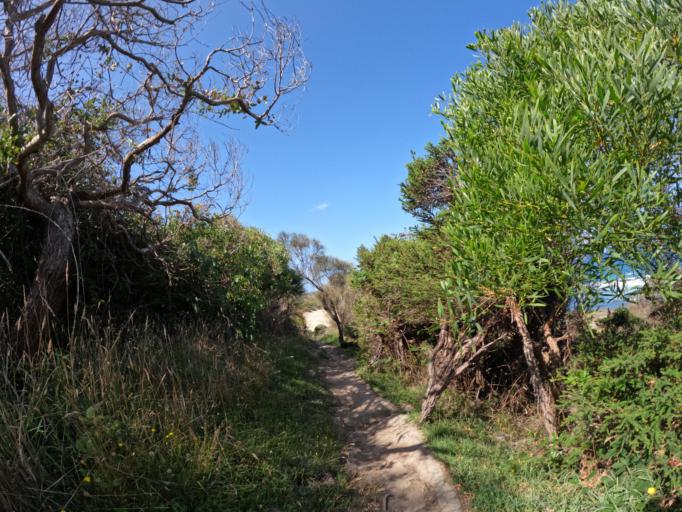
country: AU
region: Victoria
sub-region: Colac-Otway
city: Apollo Bay
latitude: -38.7892
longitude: 143.6488
